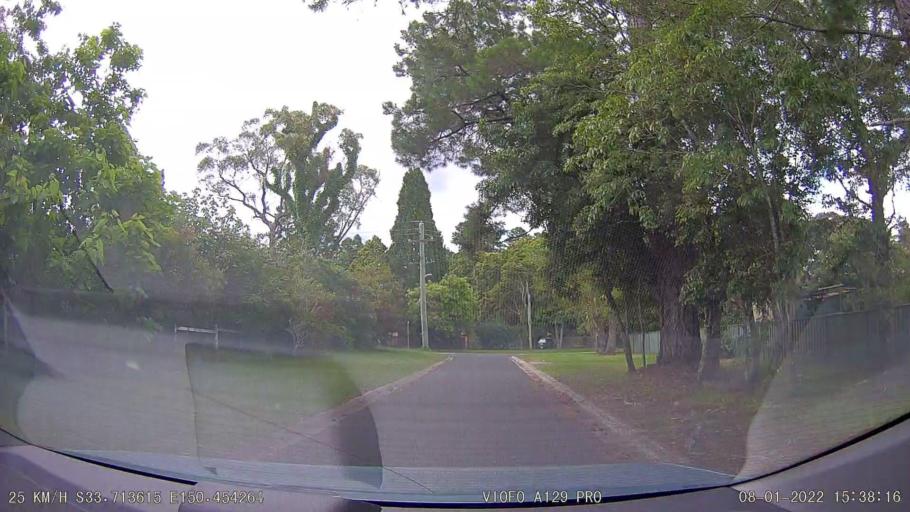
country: AU
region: New South Wales
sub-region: Blue Mountains Municipality
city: Hazelbrook
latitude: -33.7137
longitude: 150.4544
